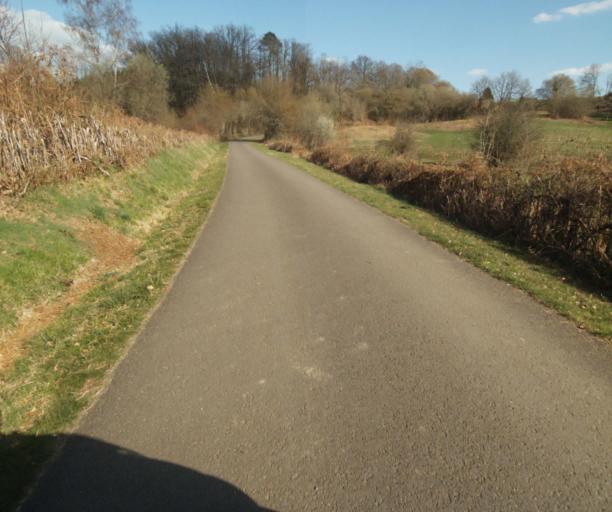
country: FR
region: Limousin
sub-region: Departement de la Correze
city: Saint-Mexant
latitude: 45.3218
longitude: 1.6188
